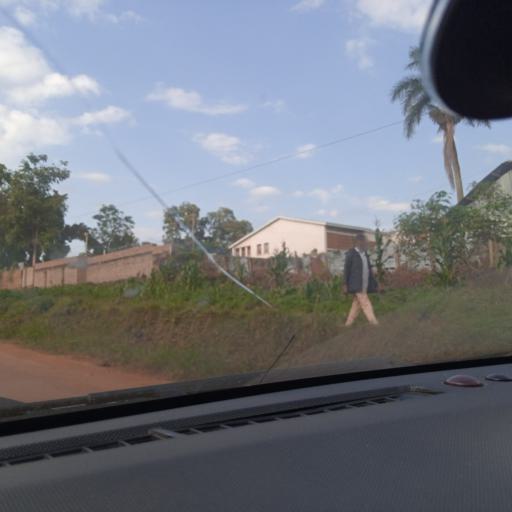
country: UG
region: Central Region
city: Masaka
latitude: -0.3512
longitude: 31.7403
